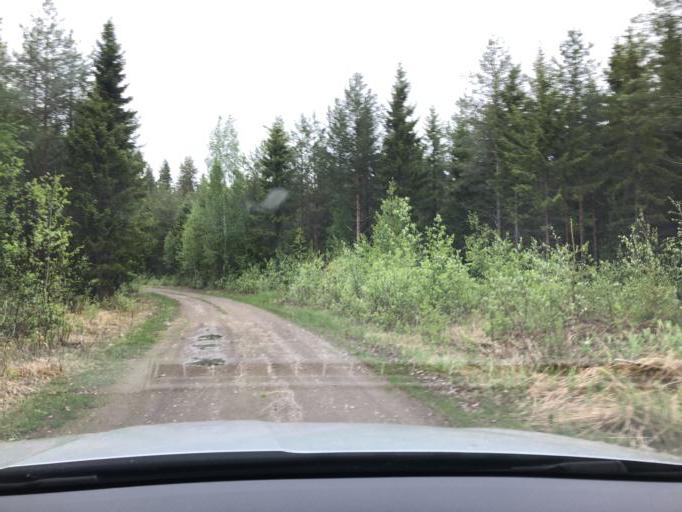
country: SE
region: Norrbotten
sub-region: Pitea Kommun
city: Roknas
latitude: 65.3930
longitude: 21.2690
